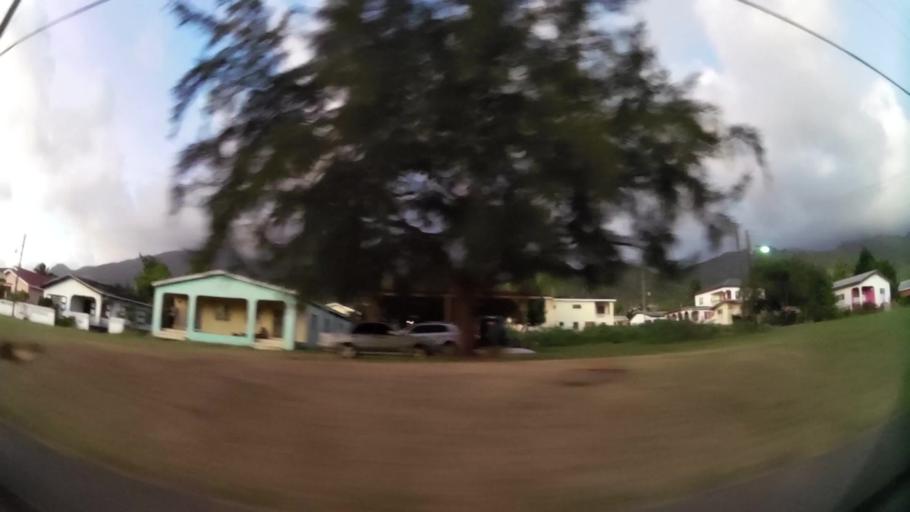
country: KN
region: Saint Thomas Middle Island
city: Middle Island
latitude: 17.3236
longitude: -62.8064
